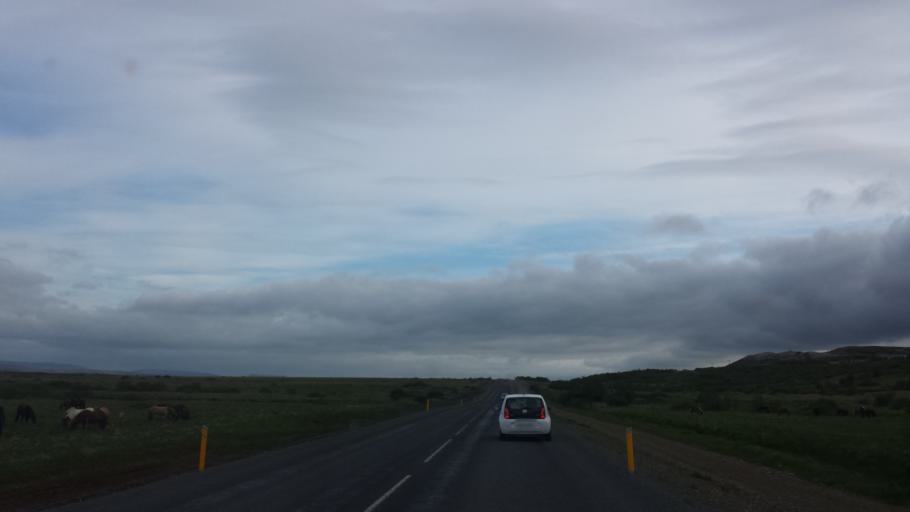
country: IS
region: South
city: Selfoss
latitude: 64.2935
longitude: -20.3356
